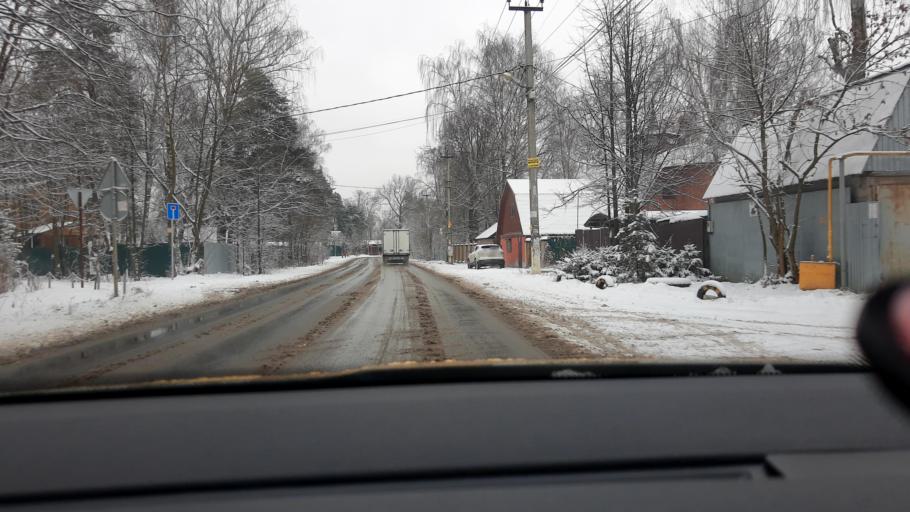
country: RU
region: Moskovskaya
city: Mamontovka
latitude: 55.9689
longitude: 37.8298
